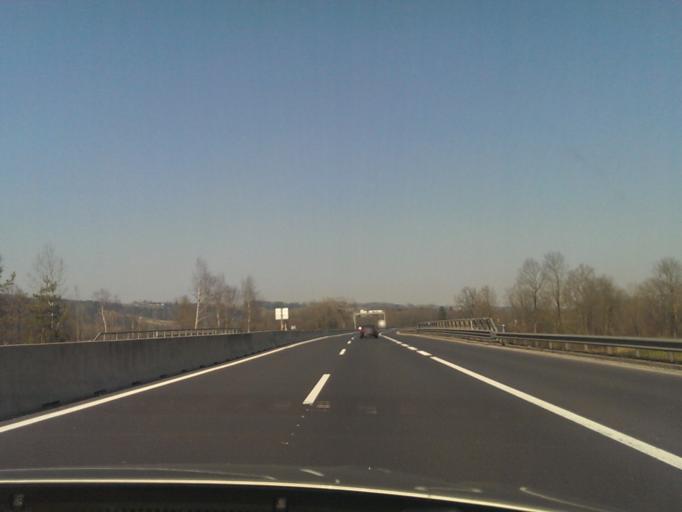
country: AT
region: Upper Austria
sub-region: Politischer Bezirk Kirchdorf an der Krems
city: Micheldorf in Oberoesterreich
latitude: 47.9306
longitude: 14.0974
